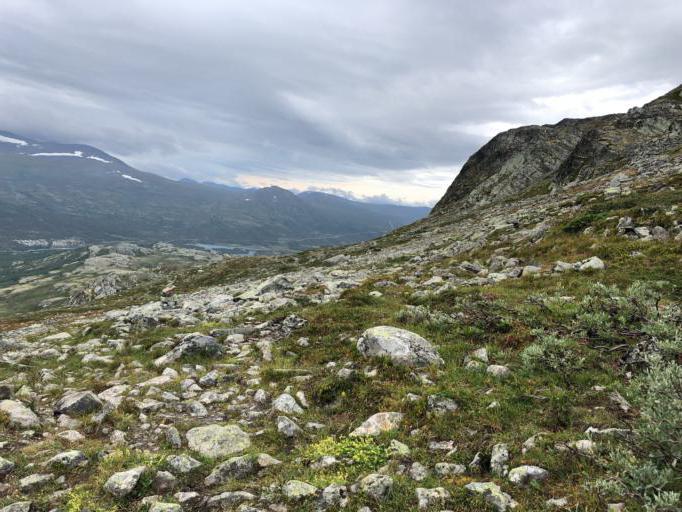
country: NO
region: Oppland
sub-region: Lom
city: Fossbergom
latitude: 61.5162
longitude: 8.8147
